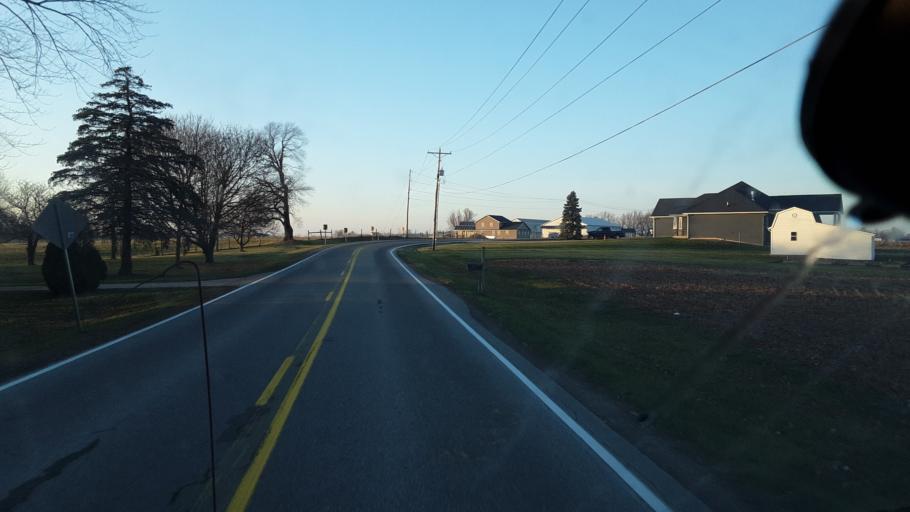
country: US
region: Indiana
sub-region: Allen County
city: Harlan
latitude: 41.1870
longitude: -84.9402
